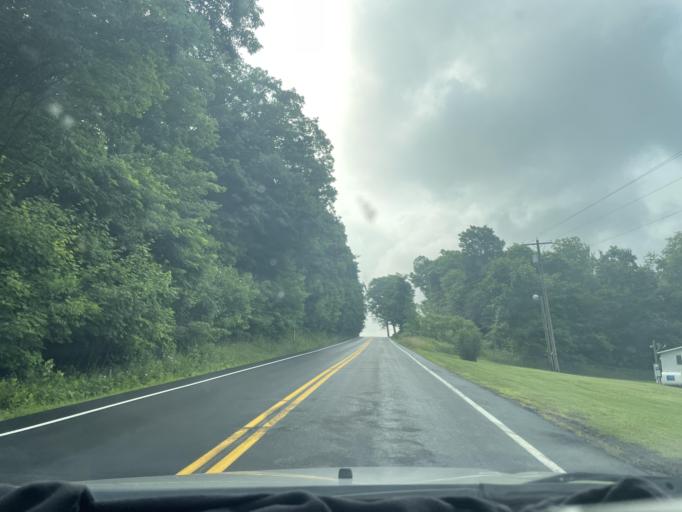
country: US
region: Maryland
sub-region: Garrett County
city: Mountain Lake Park
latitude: 39.3011
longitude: -79.3922
